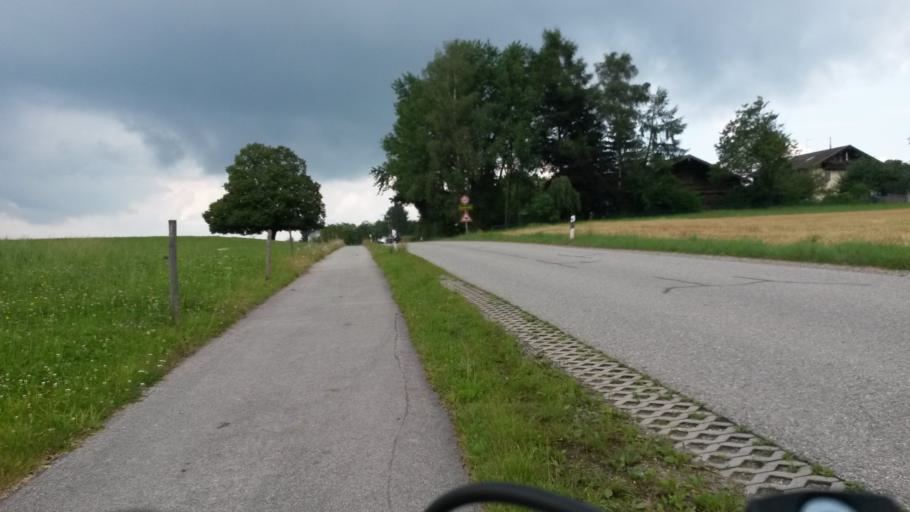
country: DE
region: Bavaria
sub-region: Upper Bavaria
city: Hoslwang
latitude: 47.9638
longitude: 12.3232
